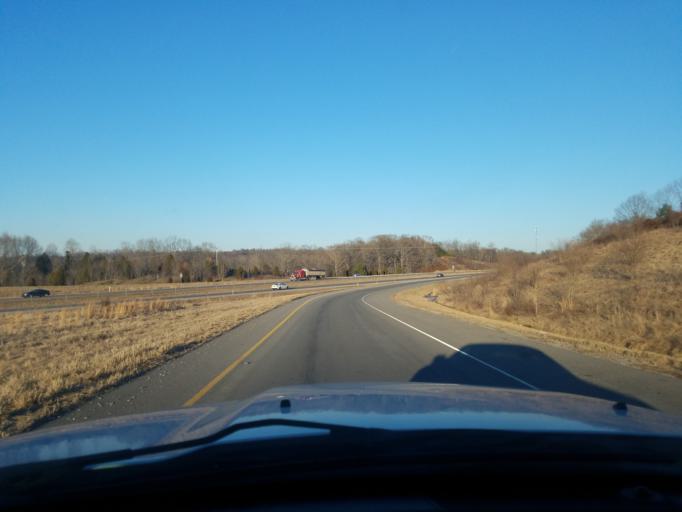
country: US
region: Indiana
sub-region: Crawford County
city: English
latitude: 38.2256
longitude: -86.5899
